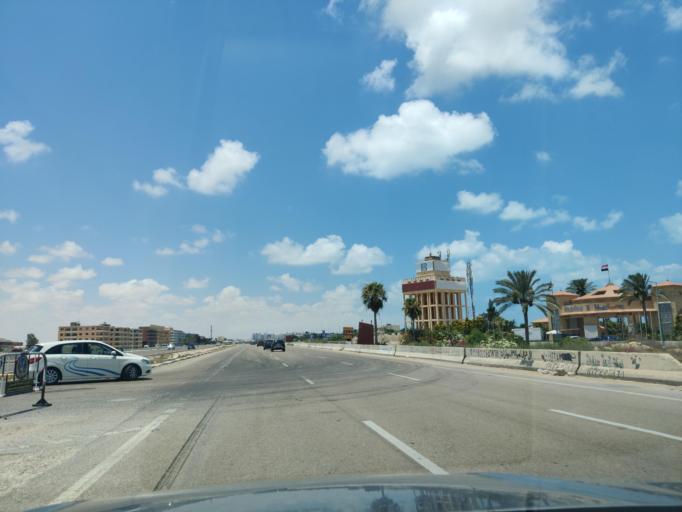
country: EG
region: Muhafazat Matruh
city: Al `Alamayn
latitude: 30.8169
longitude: 29.0319
